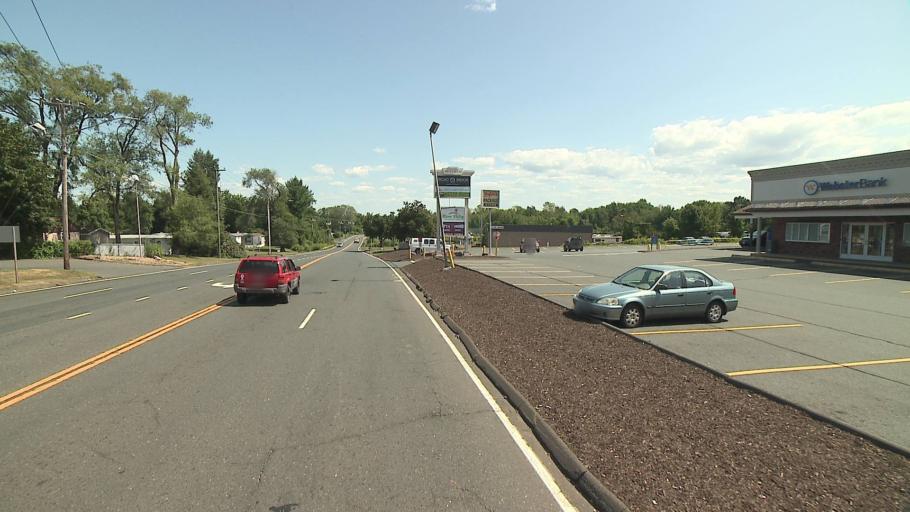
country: US
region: Connecticut
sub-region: Hartford County
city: Windsor Locks
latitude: 41.9308
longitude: -72.6045
